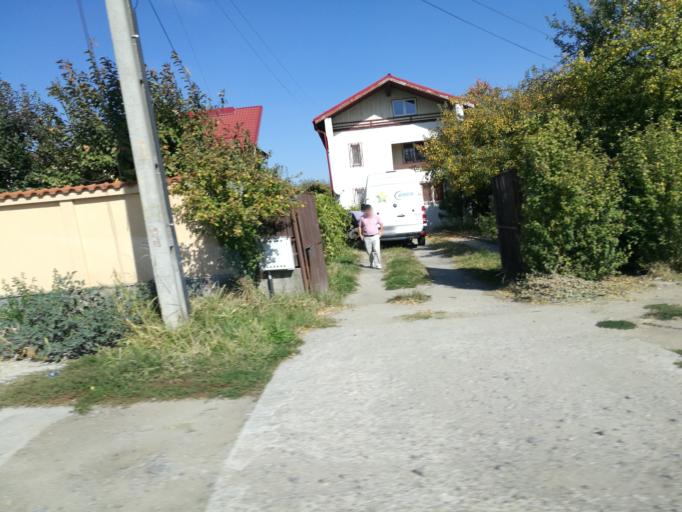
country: RO
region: Ilfov
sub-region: Comuna Dragomiresti-Vale
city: Dragomiresti-Vale
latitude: 44.4664
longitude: 25.9263
